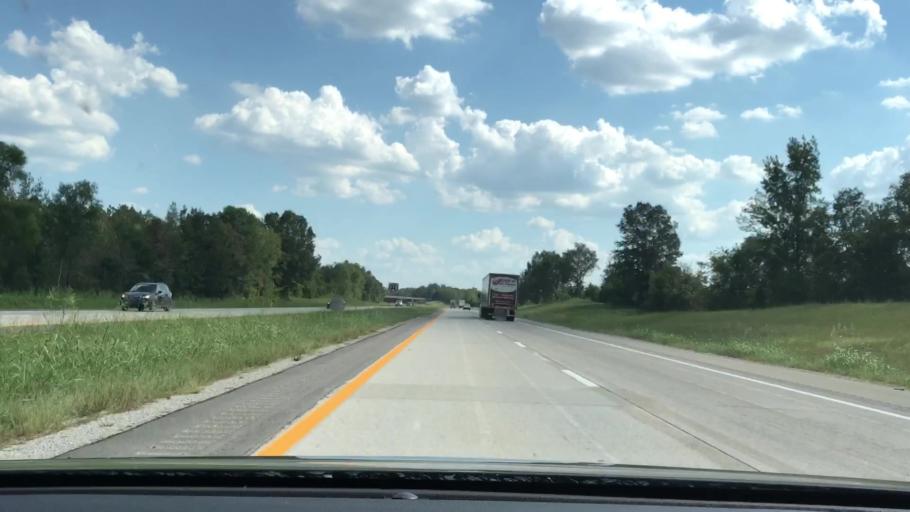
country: US
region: Kentucky
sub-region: Ohio County
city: Oak Grove
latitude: 37.3573
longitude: -86.7907
